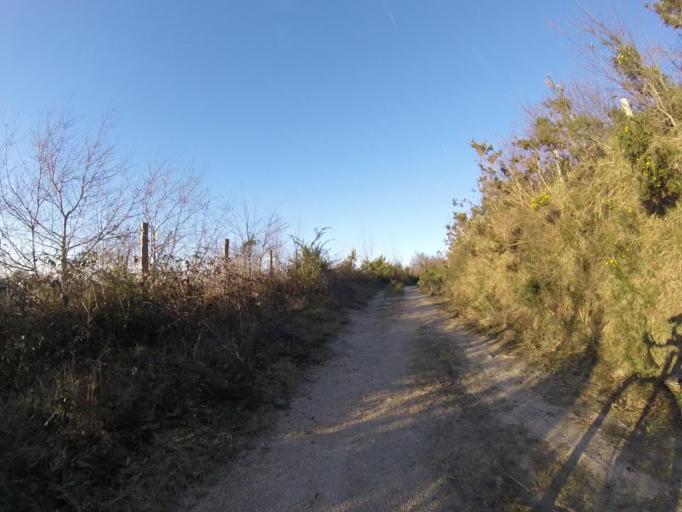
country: ES
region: Navarre
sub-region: Provincia de Navarra
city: Arano
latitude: 43.2575
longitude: -1.8404
